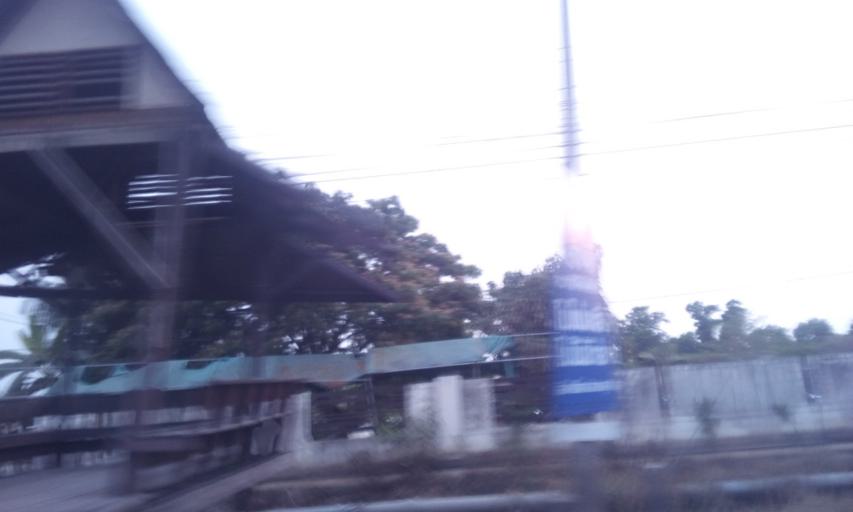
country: TH
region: Bangkok
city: Nong Chok
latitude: 13.8354
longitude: 100.9078
